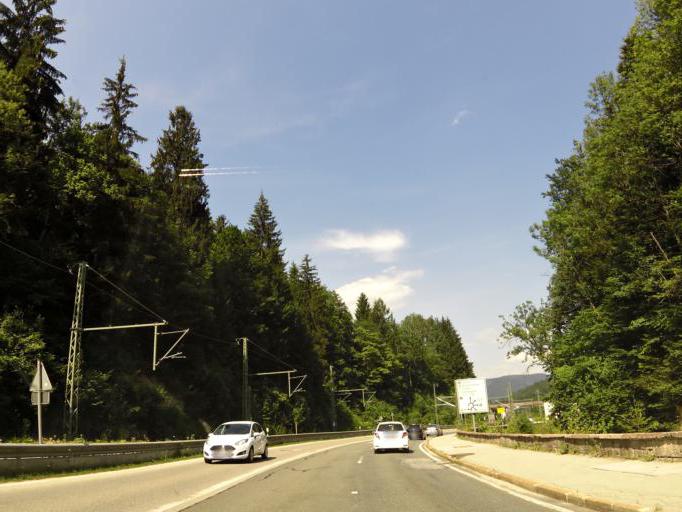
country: DE
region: Bavaria
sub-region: Upper Bavaria
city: Berchtesgaden
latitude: 47.6251
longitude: 12.9954
